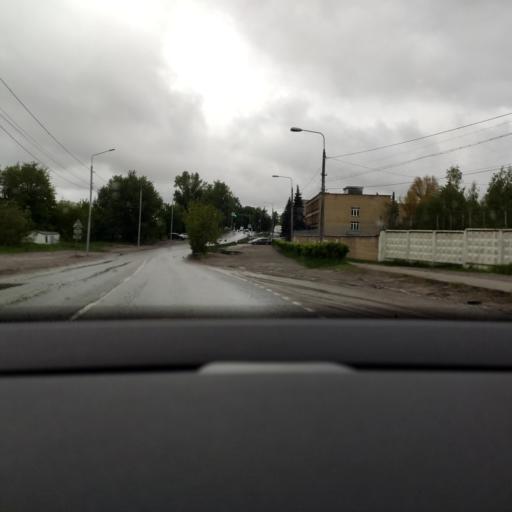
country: RU
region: Moskovskaya
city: Saltykovka
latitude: 55.7354
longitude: 37.9683
